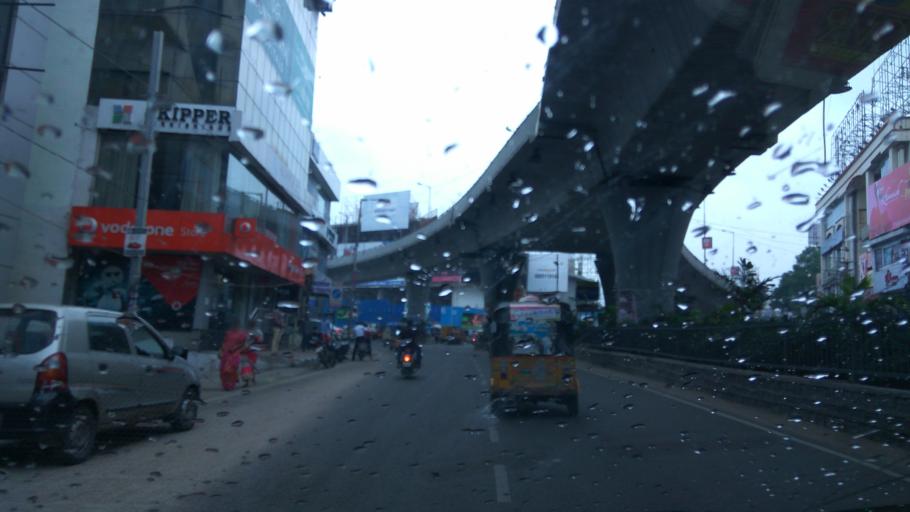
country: IN
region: Telangana
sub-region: Hyderabad
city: Hyderabad
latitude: 17.4258
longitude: 78.4496
